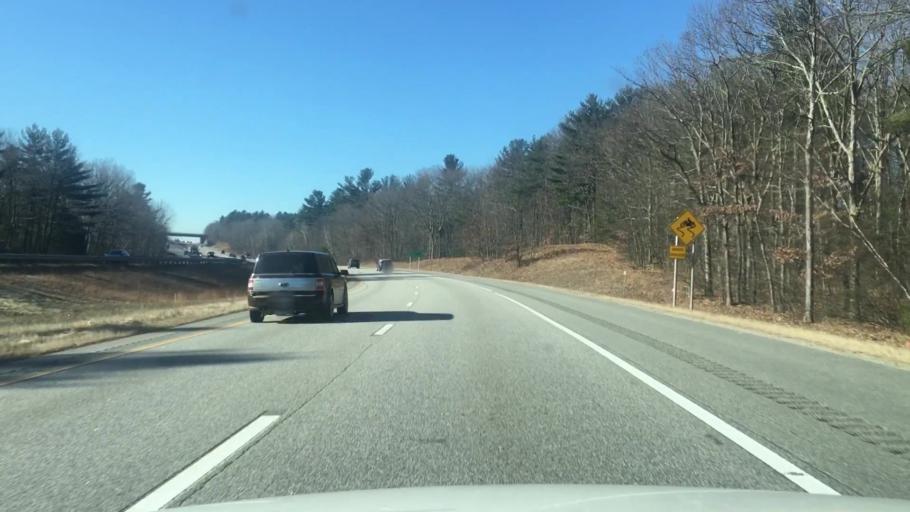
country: US
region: New Hampshire
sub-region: Rockingham County
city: Auburn
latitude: 43.0374
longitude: -71.3293
